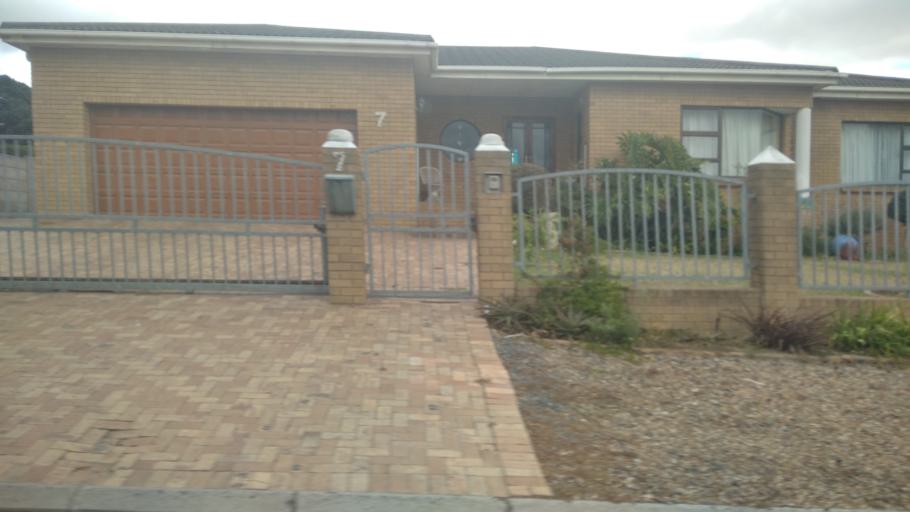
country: ZA
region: Western Cape
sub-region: City of Cape Town
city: Kraaifontein
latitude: -33.8199
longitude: 18.6843
